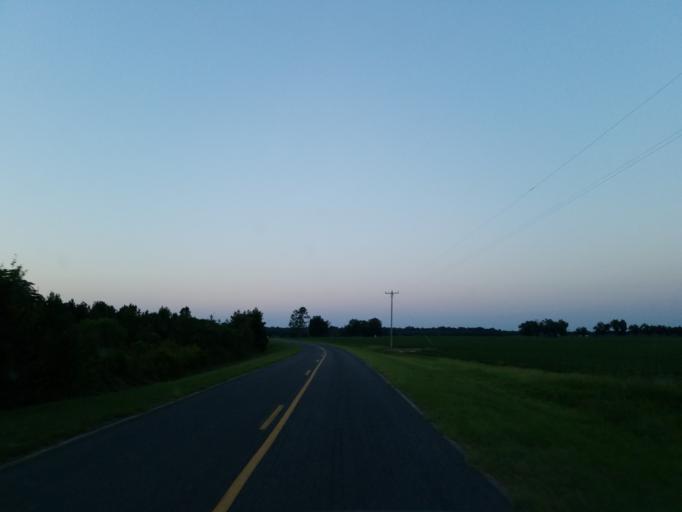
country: US
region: Georgia
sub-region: Dooly County
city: Unadilla
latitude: 32.2178
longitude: -83.7962
